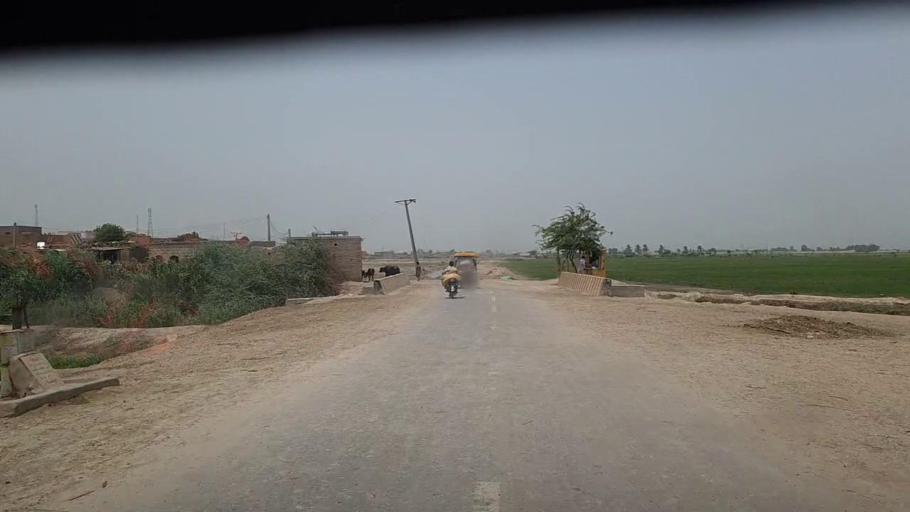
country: PK
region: Sindh
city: Sita Road
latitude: 27.0417
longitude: 67.8583
